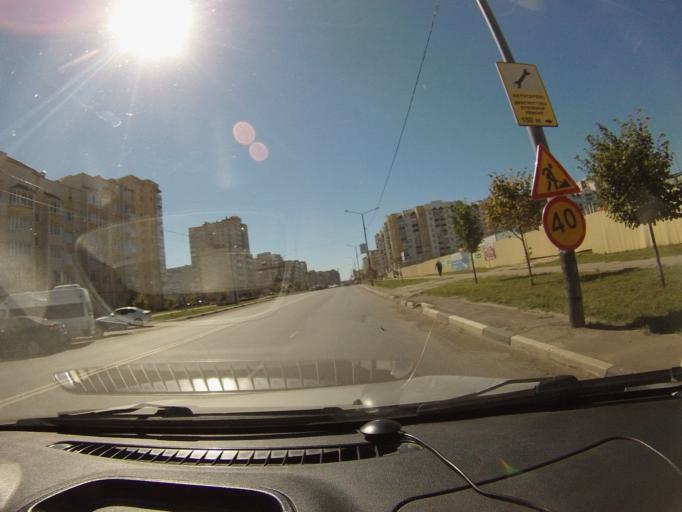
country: RU
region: Tambov
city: Tambov
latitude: 52.7704
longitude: 41.4076
